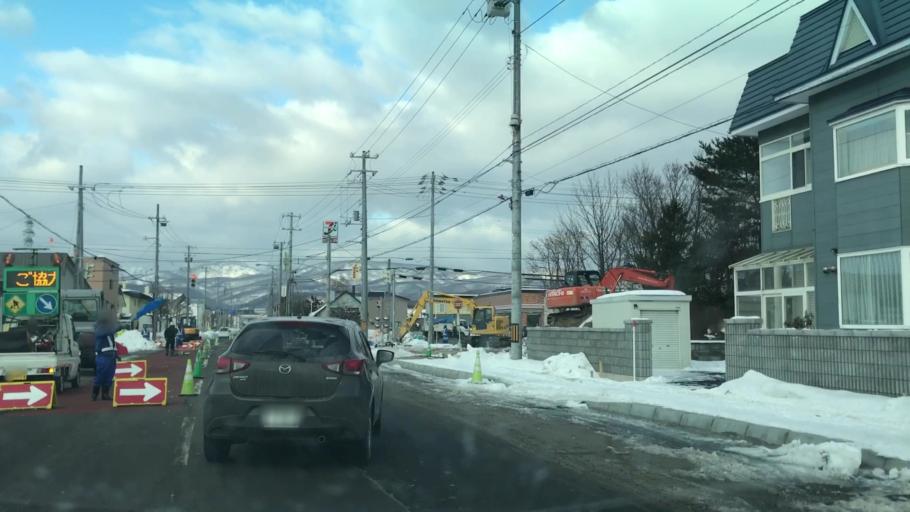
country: JP
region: Hokkaido
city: Yoichi
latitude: 43.1829
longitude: 140.8053
